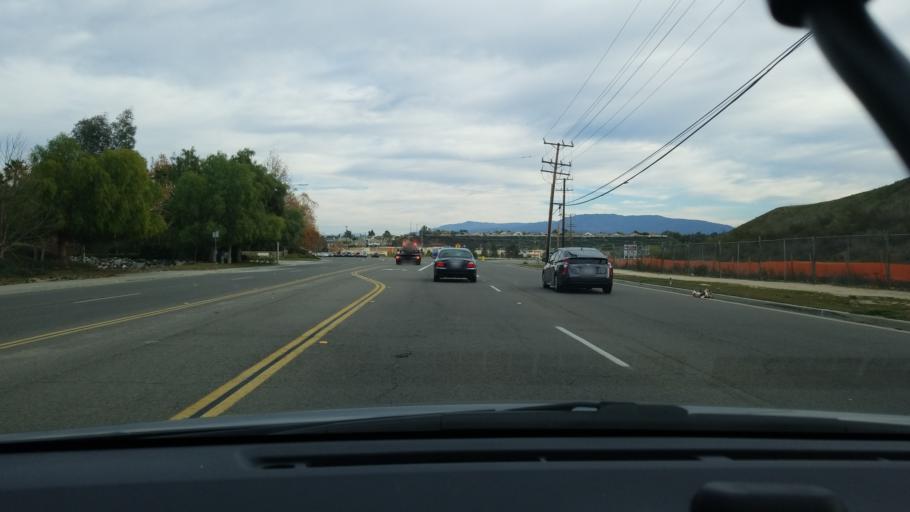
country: US
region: California
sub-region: Riverside County
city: Murrieta Hot Springs
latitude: 33.5538
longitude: -117.1442
